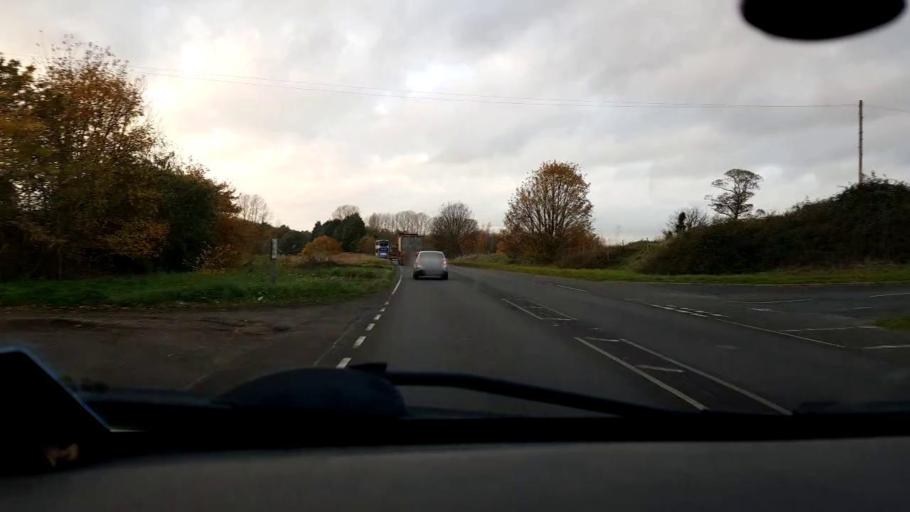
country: GB
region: England
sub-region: Norfolk
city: Costessey
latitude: 52.7043
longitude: 1.1551
